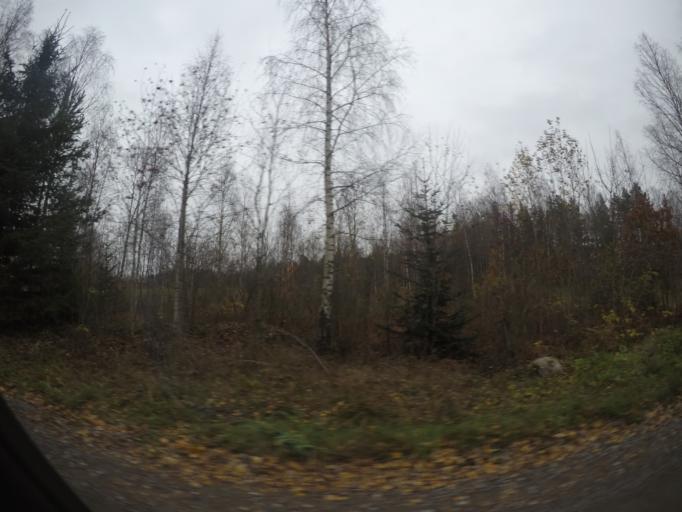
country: SE
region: Vaestmanland
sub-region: Kopings Kommun
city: Koping
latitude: 59.5904
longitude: 16.0868
